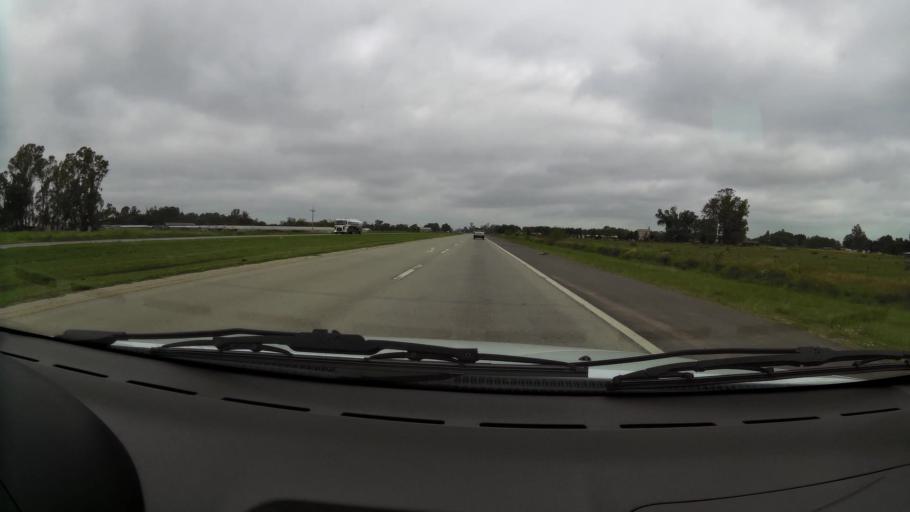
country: AR
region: Buenos Aires
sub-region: Partido de Brandsen
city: Brandsen
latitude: -35.0496
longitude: -58.1221
